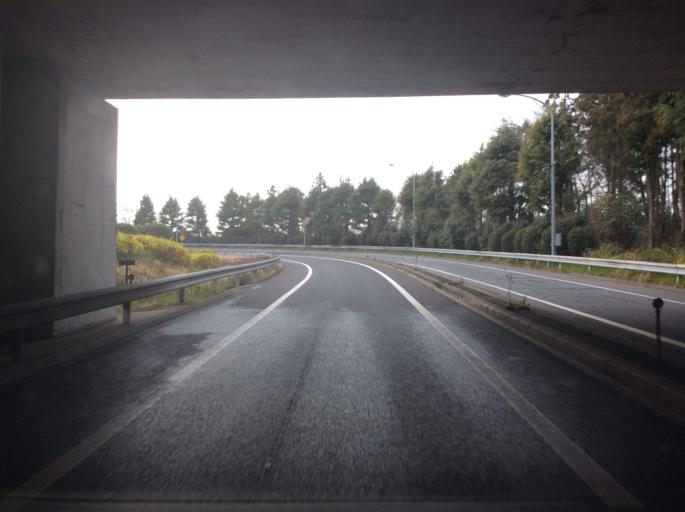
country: JP
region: Ibaraki
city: Naka
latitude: 36.1198
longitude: 140.1851
